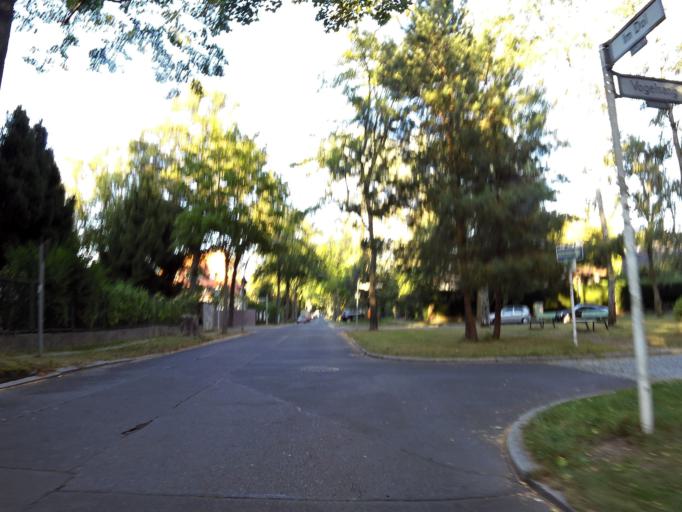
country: DE
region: Berlin
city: Dahlem
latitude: 52.4629
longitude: 13.2813
